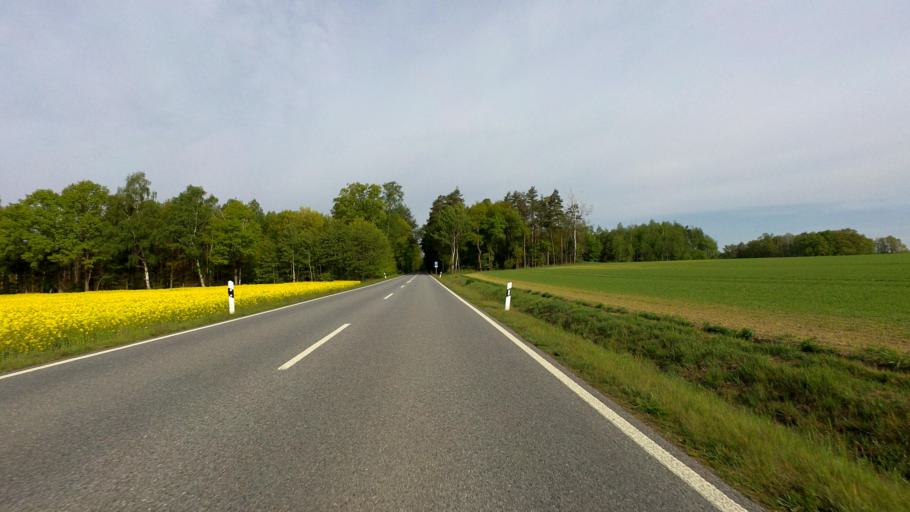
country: DE
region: Saxony
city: Stolpen
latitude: 51.0696
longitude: 14.0456
